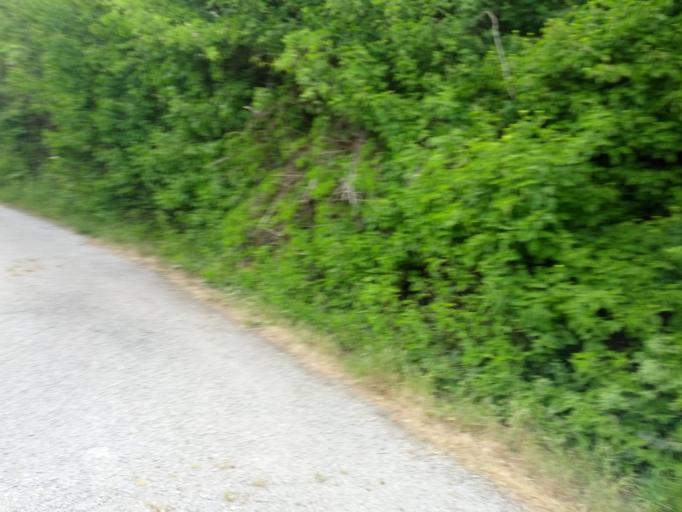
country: DE
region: Thuringia
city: Eisenach
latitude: 50.9963
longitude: 10.3001
